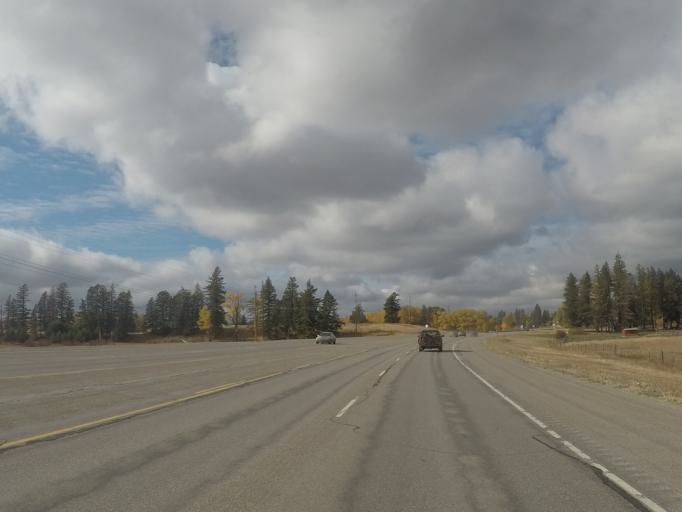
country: US
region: Montana
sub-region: Flathead County
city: Columbia Falls
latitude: 48.3637
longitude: -114.1608
